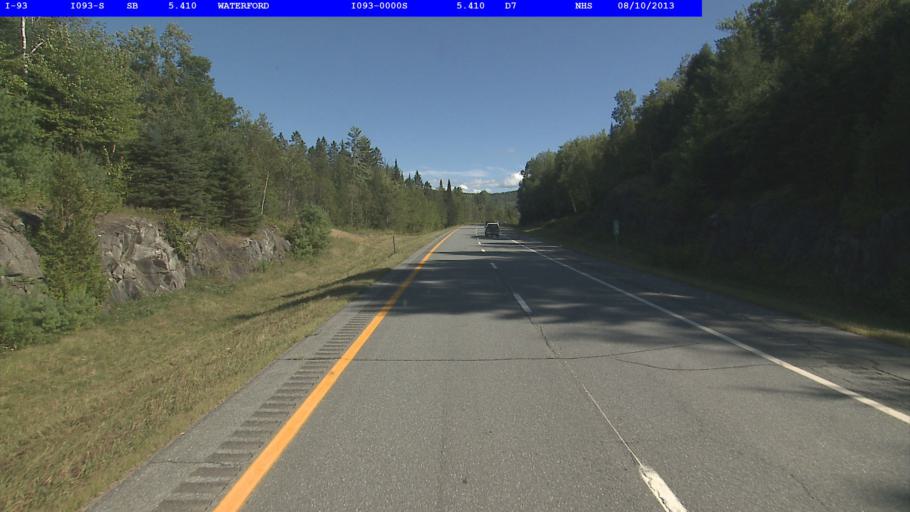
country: US
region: Vermont
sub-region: Caledonia County
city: Saint Johnsbury
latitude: 44.4129
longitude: -71.9233
